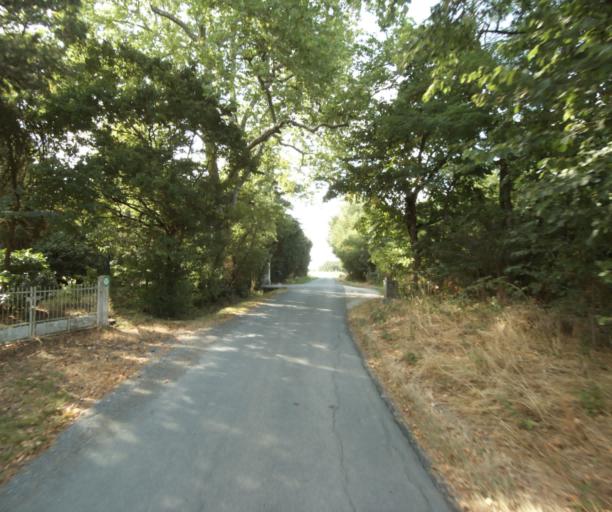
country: FR
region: Midi-Pyrenees
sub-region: Departement de la Haute-Garonne
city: Revel
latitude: 43.5000
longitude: 1.9800
